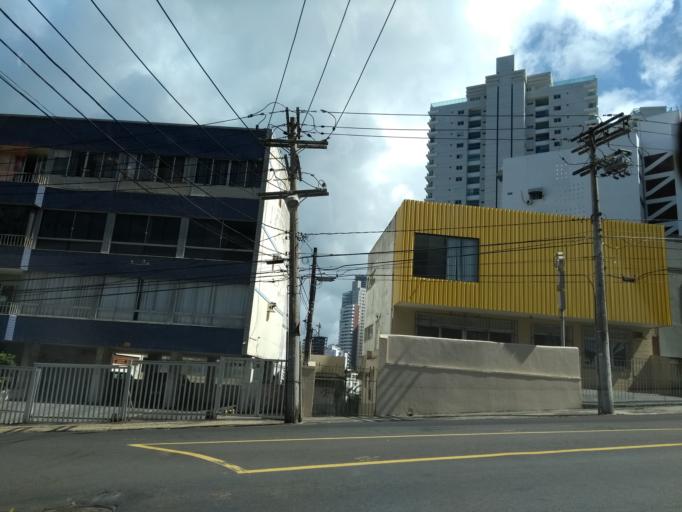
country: BR
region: Bahia
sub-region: Salvador
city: Salvador
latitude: -13.0038
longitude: -38.5272
